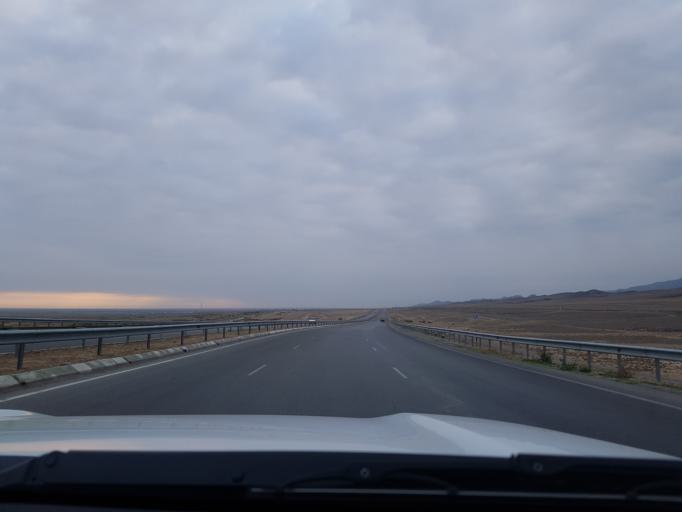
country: IR
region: Razavi Khorasan
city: Dargaz
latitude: 37.6820
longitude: 59.0837
